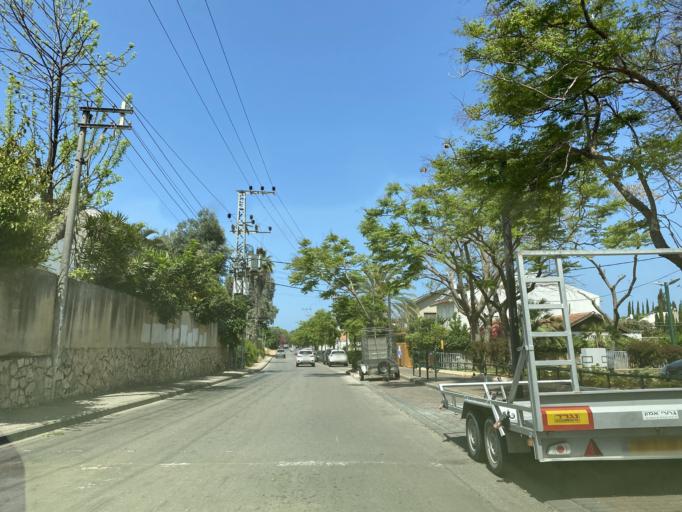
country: IL
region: Tel Aviv
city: Ramat HaSharon
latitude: 32.1531
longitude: 34.8384
